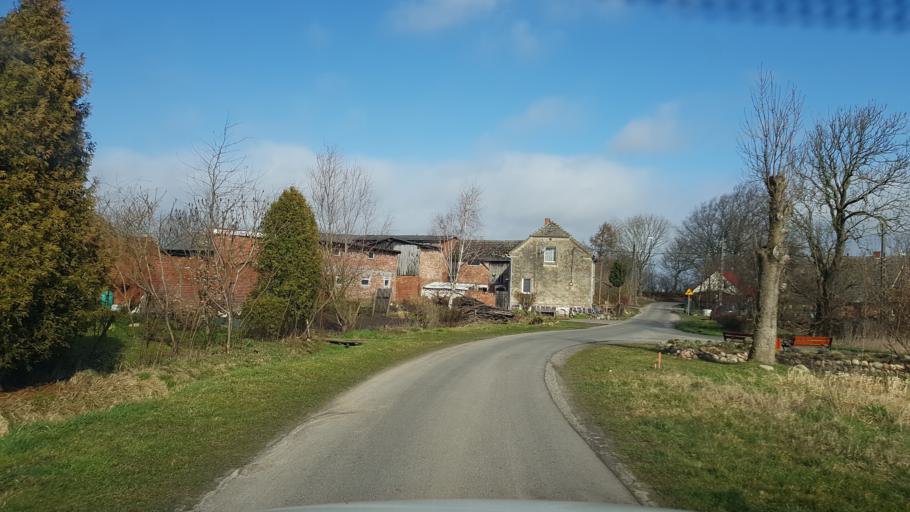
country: PL
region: West Pomeranian Voivodeship
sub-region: Powiat slawienski
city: Slawno
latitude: 54.4802
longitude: 16.6505
